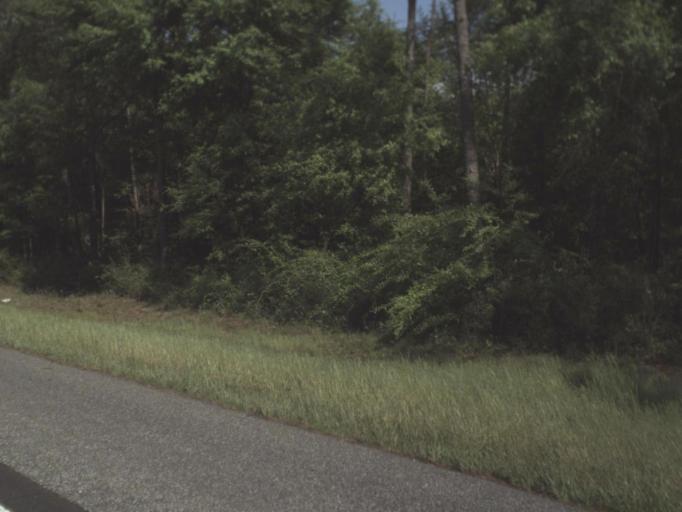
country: US
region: Florida
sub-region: Santa Rosa County
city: East Milton
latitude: 30.6520
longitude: -86.8861
